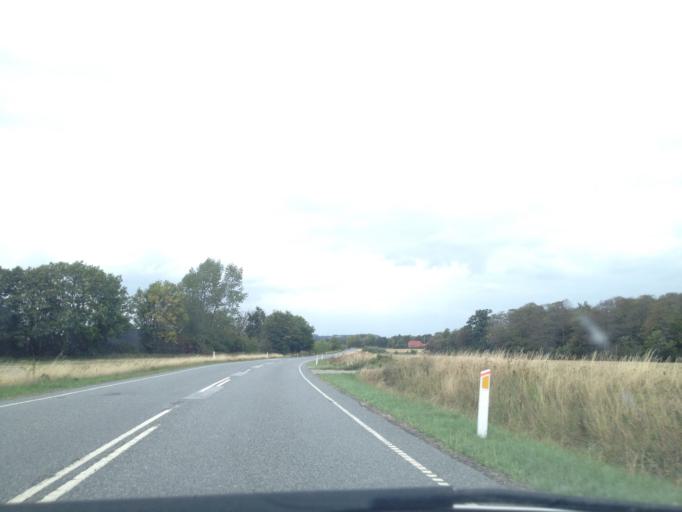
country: DK
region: South Denmark
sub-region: Haderslev Kommune
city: Starup
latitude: 55.2867
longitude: 9.5579
